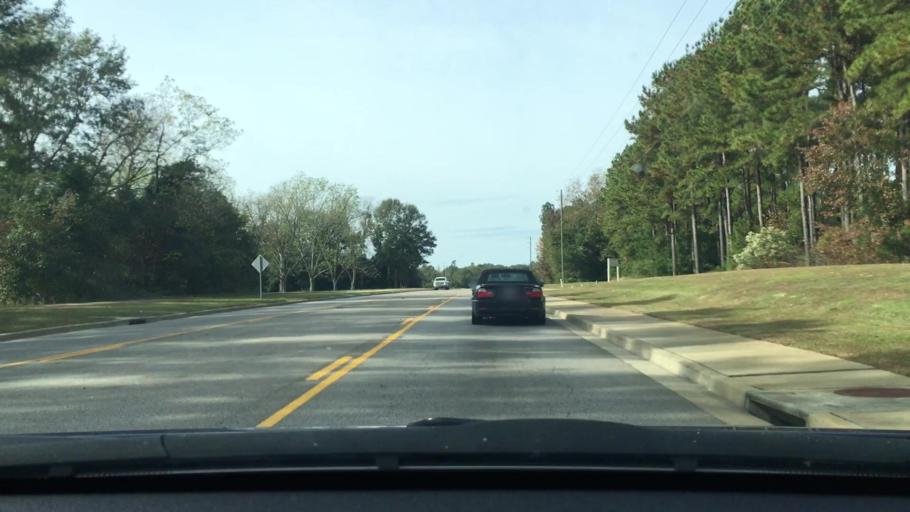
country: US
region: South Carolina
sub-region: Sumter County
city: South Sumter
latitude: 33.9205
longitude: -80.3953
